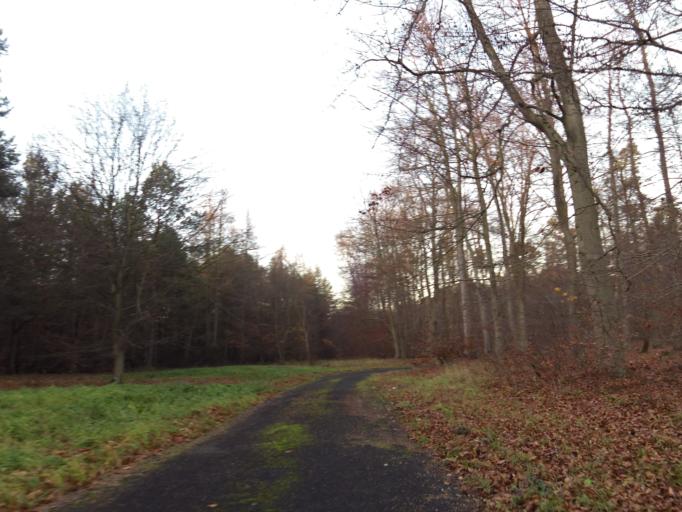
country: DE
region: Hesse
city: Morfelden-Walldorf
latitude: 49.9981
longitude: 8.6071
